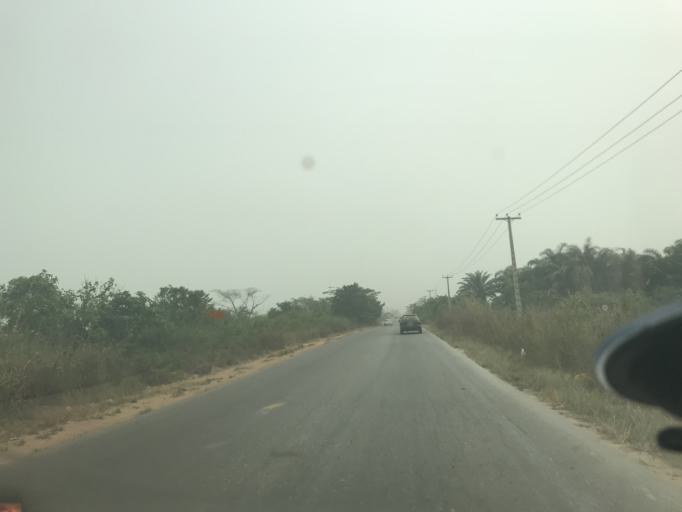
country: NG
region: Ogun
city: Itori
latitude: 6.8902
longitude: 3.1747
